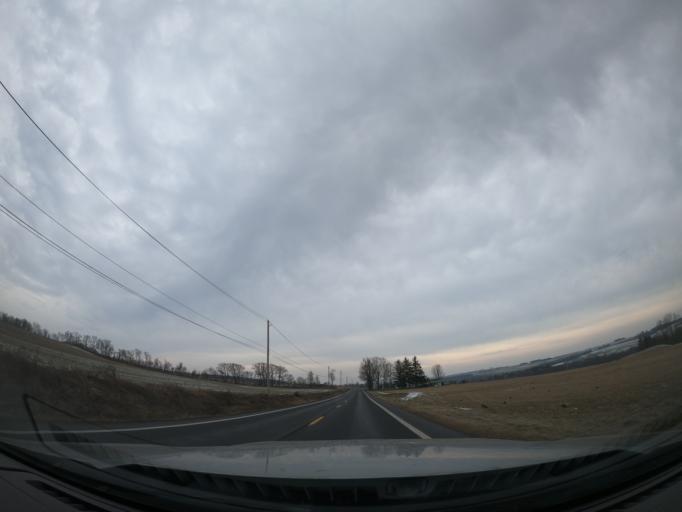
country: US
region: New York
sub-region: Cayuga County
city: Moravia
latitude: 42.7577
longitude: -76.5567
